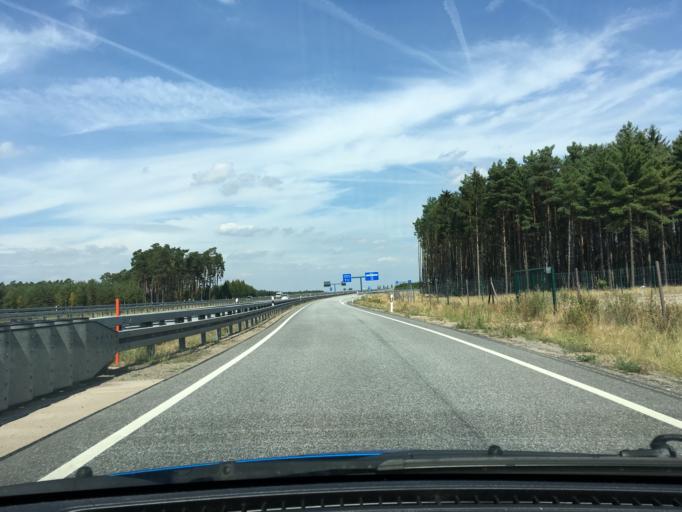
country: DE
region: Mecklenburg-Vorpommern
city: Gross Laasch
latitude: 53.4179
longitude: 11.5222
